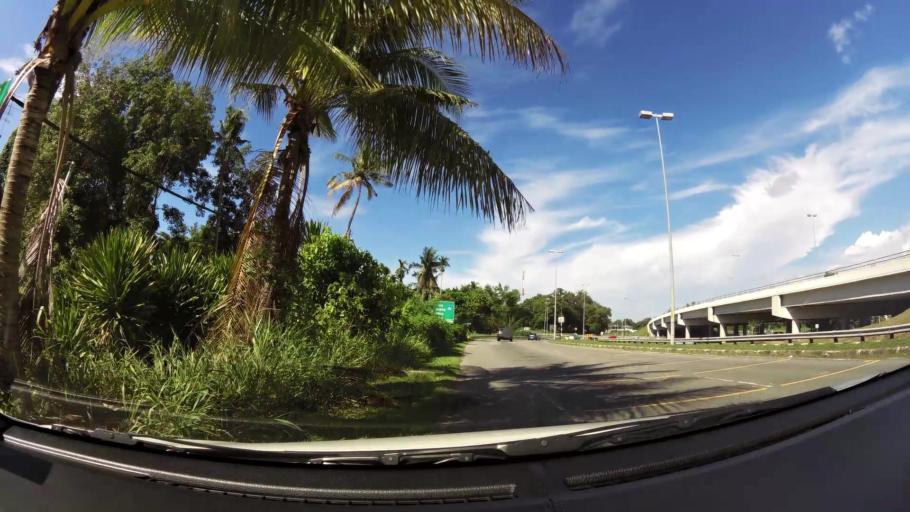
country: BN
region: Brunei and Muara
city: Bandar Seri Begawan
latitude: 4.9508
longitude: 114.9432
